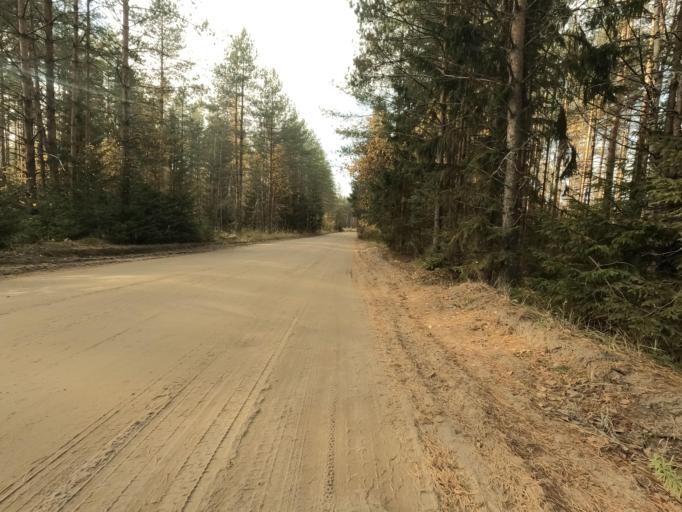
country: RU
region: Leningrad
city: Priladozhskiy
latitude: 59.6310
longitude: 31.3924
